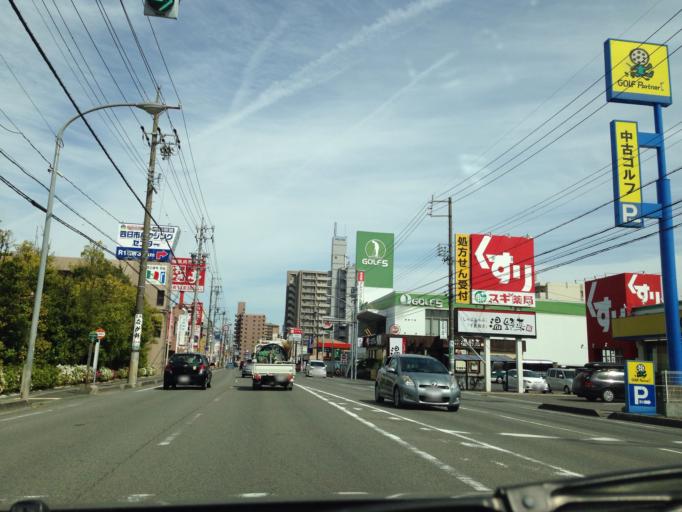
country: JP
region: Mie
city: Yokkaichi
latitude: 34.9742
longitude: 136.6087
